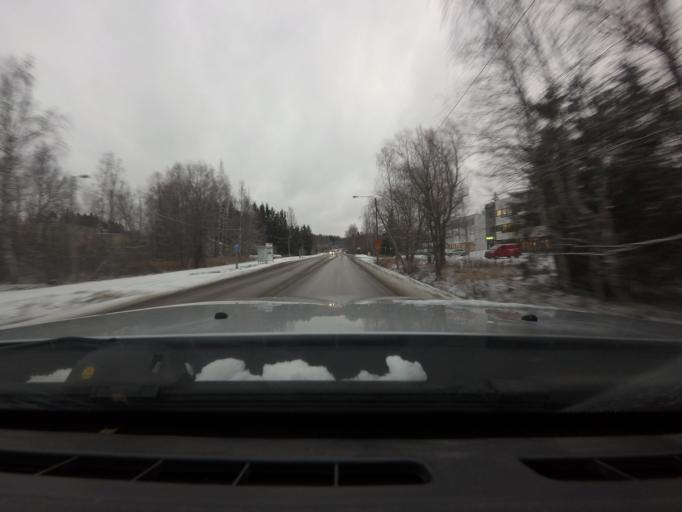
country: FI
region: Uusimaa
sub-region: Helsinki
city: Kauniainen
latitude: 60.2251
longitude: 24.7357
